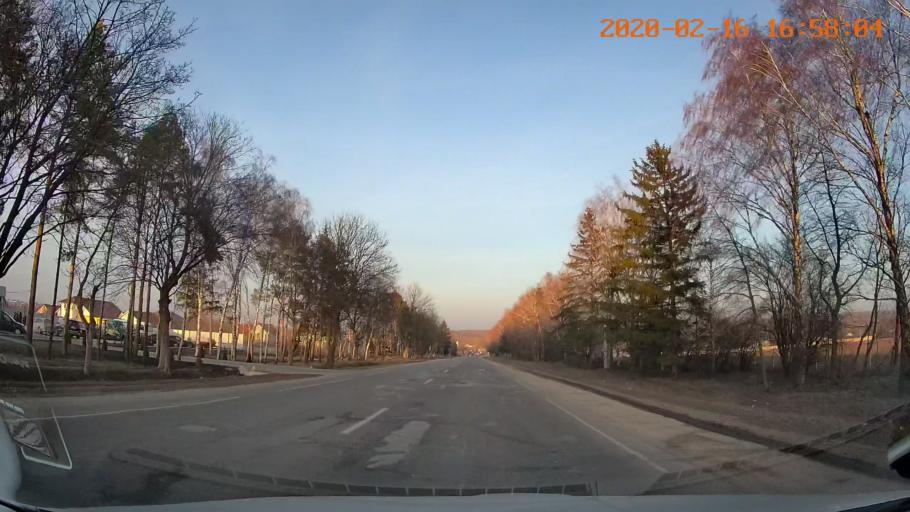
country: MD
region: Briceni
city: Briceni
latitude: 48.3481
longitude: 27.0779
